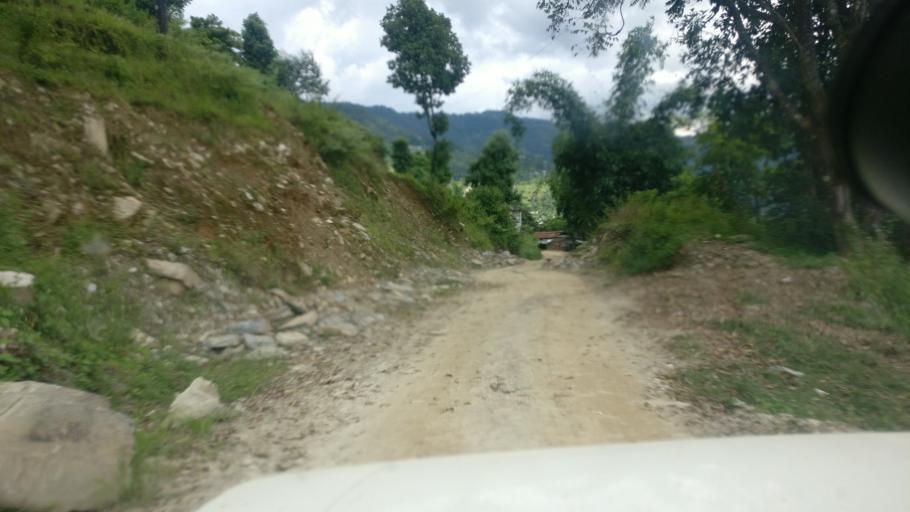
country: NP
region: Western Region
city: Baglung
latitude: 28.2603
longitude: 83.6467
